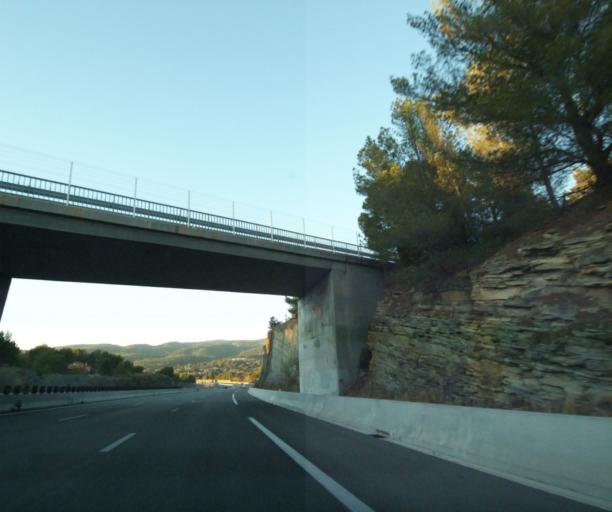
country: FR
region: Provence-Alpes-Cote d'Azur
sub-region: Departement des Bouches-du-Rhone
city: Ceyreste
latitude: 43.2027
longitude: 5.6330
